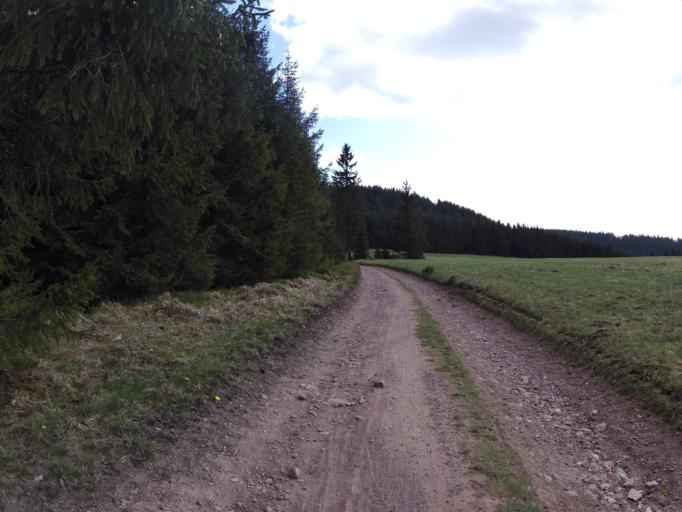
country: DE
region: Thuringia
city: Unterschonau
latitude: 50.7592
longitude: 10.5638
